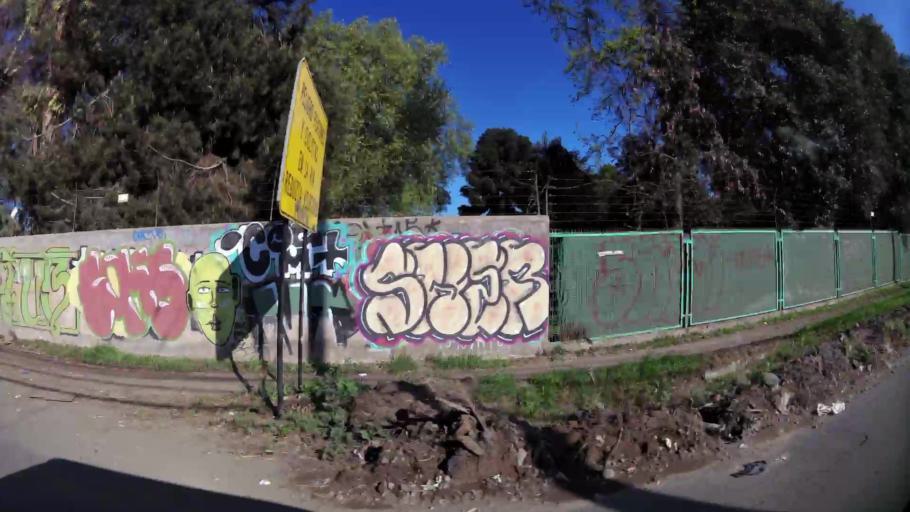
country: CL
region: Santiago Metropolitan
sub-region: Provincia de Chacabuco
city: Chicureo Abajo
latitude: -33.3704
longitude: -70.6600
